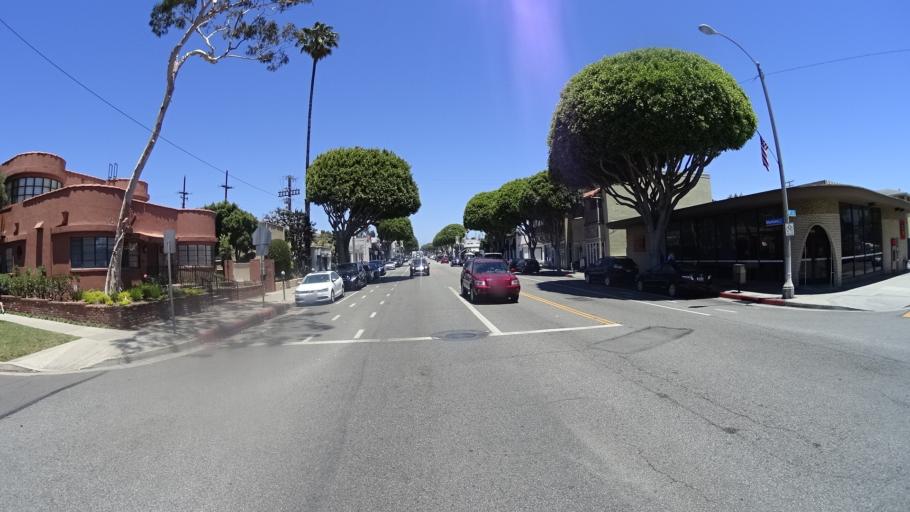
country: US
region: California
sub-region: Los Angeles County
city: Santa Monica
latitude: 34.0282
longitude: -118.5001
